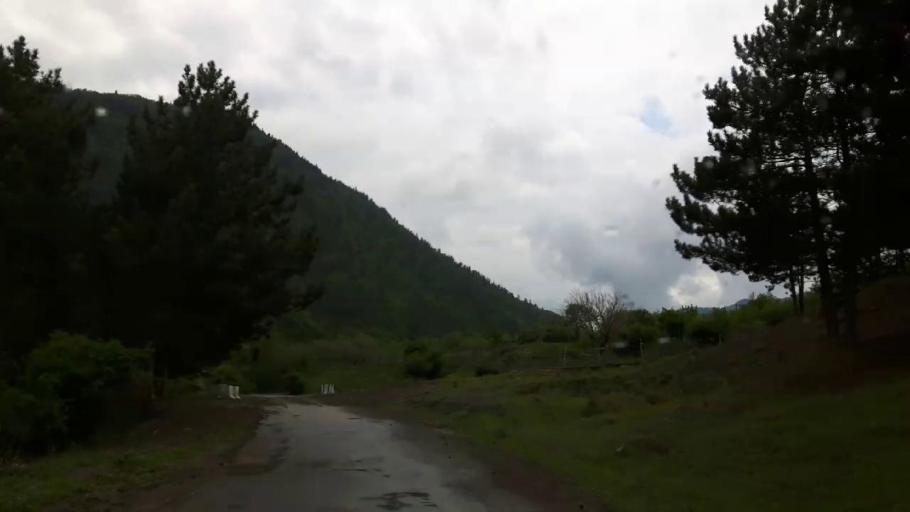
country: GE
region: Shida Kartli
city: Gori
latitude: 41.8947
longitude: 44.0260
